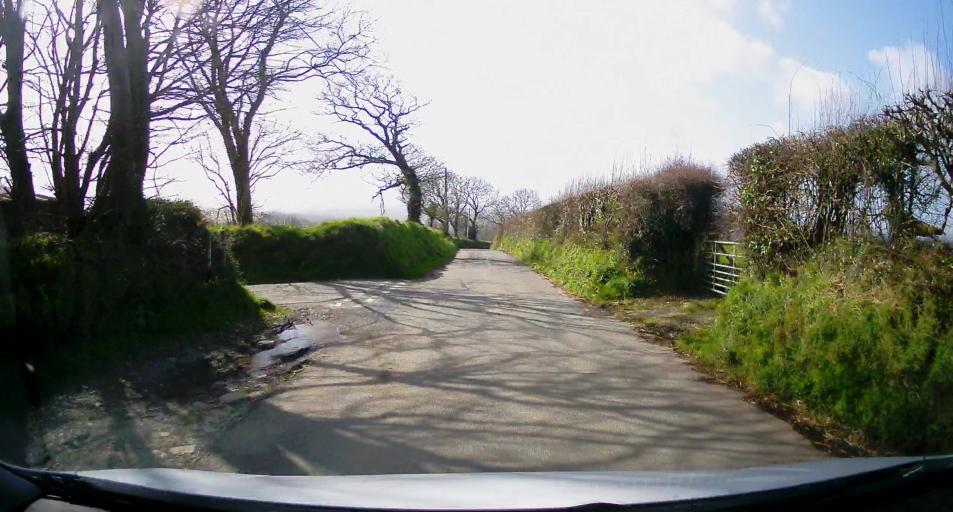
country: GB
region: Wales
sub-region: County of Ceredigion
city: Aberporth
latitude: 52.0688
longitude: -4.5679
